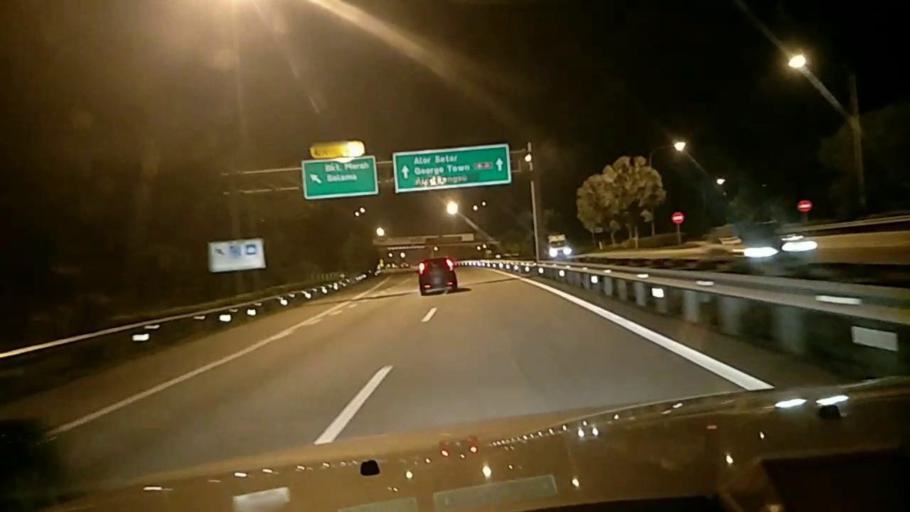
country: MY
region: Perak
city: Simpang Empat
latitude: 4.9923
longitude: 100.6593
